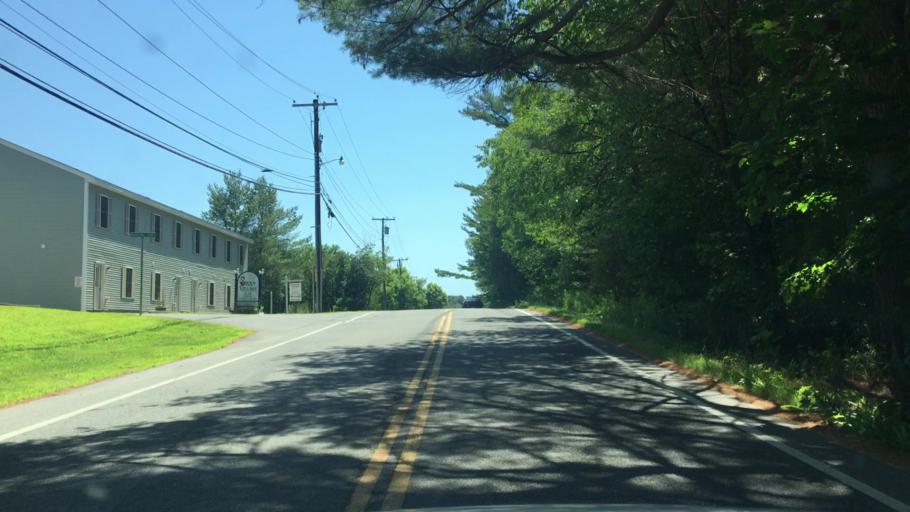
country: US
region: Maine
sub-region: Penobscot County
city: Bangor
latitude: 44.8200
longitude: -68.7919
